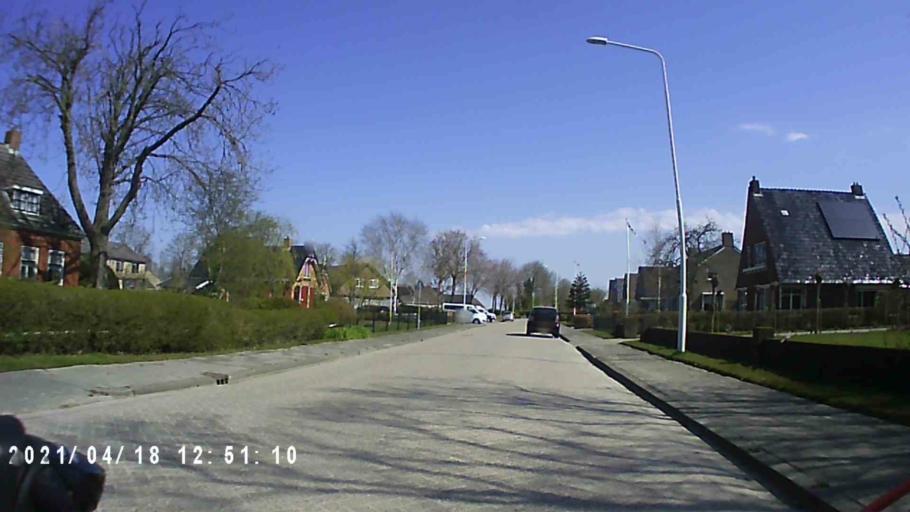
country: NL
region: Friesland
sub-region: Gemeente Dongeradeel
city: Anjum
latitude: 53.3790
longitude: 6.0569
